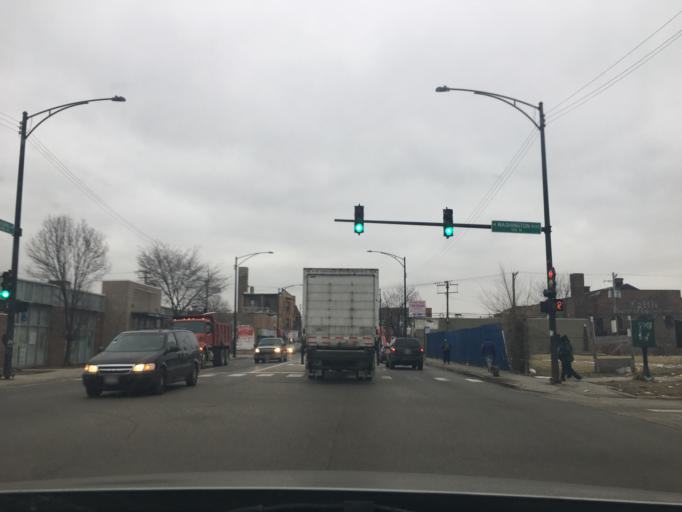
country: US
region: Illinois
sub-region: Cook County
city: Cicero
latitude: 41.8819
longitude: -87.7454
